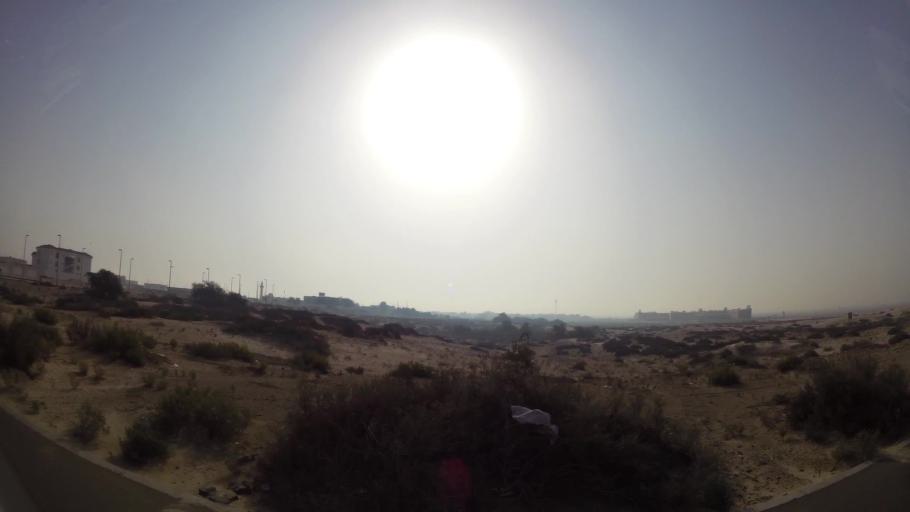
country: AE
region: Abu Dhabi
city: Abu Dhabi
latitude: 24.2696
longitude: 54.6547
